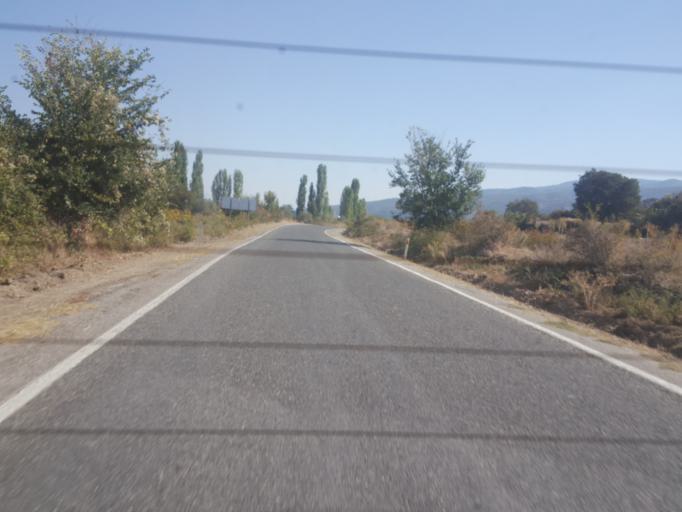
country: TR
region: Kastamonu
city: Tosya
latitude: 40.9941
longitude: 34.1292
